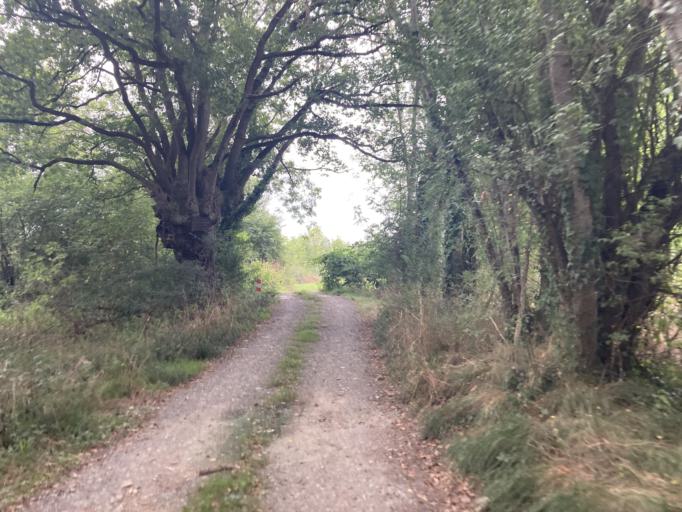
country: FR
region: Aquitaine
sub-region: Departement des Pyrenees-Atlantiques
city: Arbus
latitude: 43.3266
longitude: -0.4846
